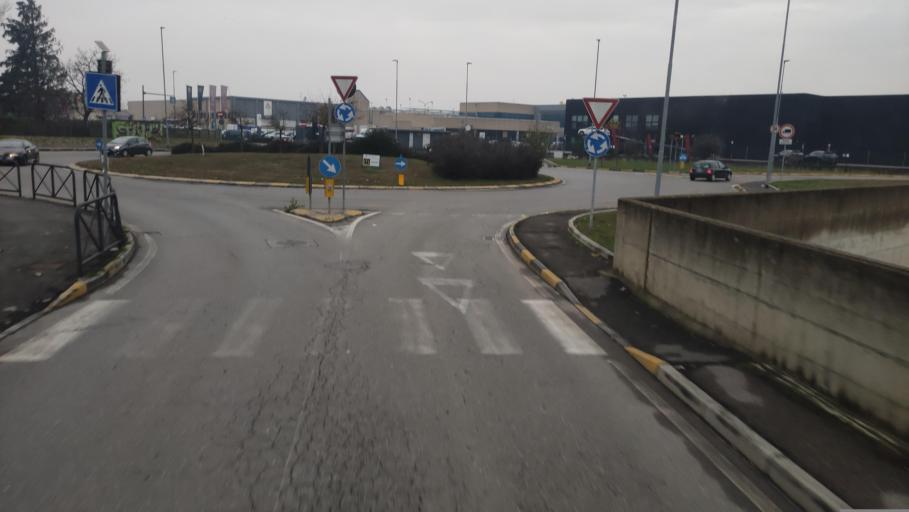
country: IT
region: Lombardy
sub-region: Provincia di Cremona
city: Bagnolo Cremasco
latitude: 45.3631
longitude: 9.6297
